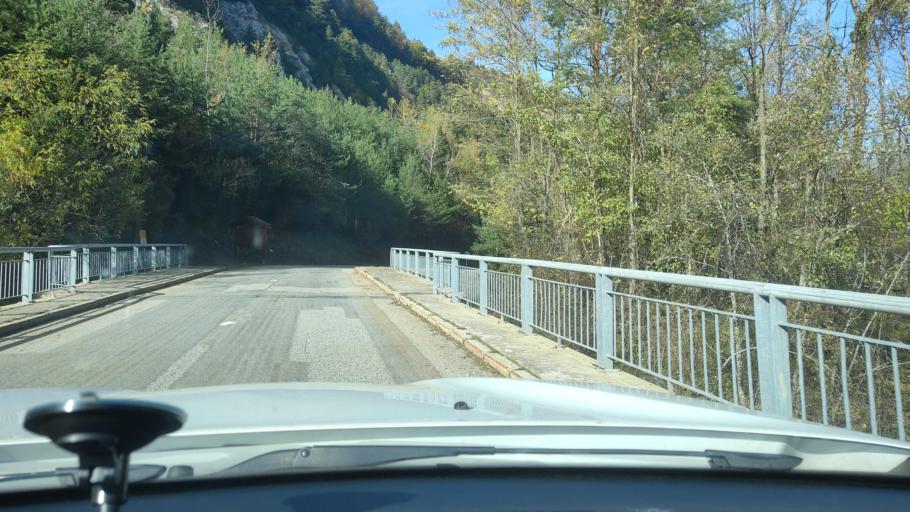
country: FR
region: Rhone-Alpes
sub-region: Departement de la Savoie
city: Saint-Jean-de-Maurienne
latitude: 45.2335
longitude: 6.3143
